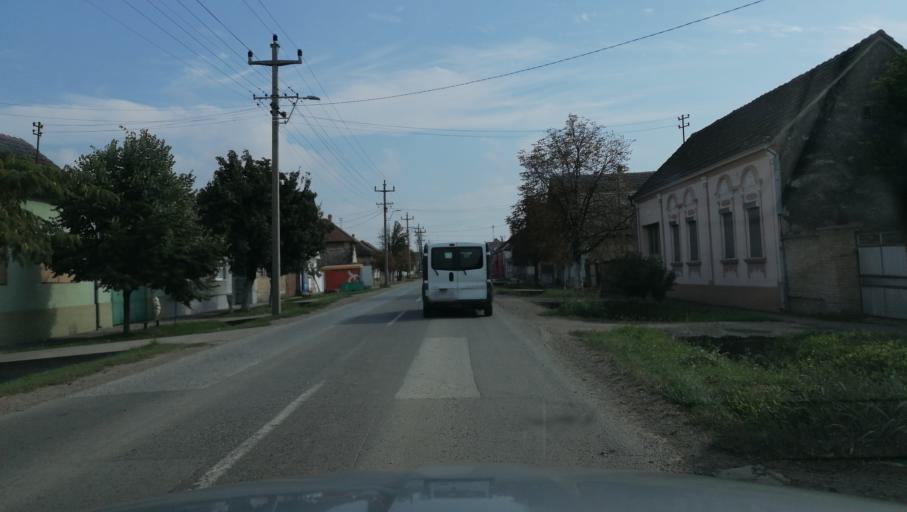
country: RS
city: Ravnje
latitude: 45.0237
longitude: 19.4012
